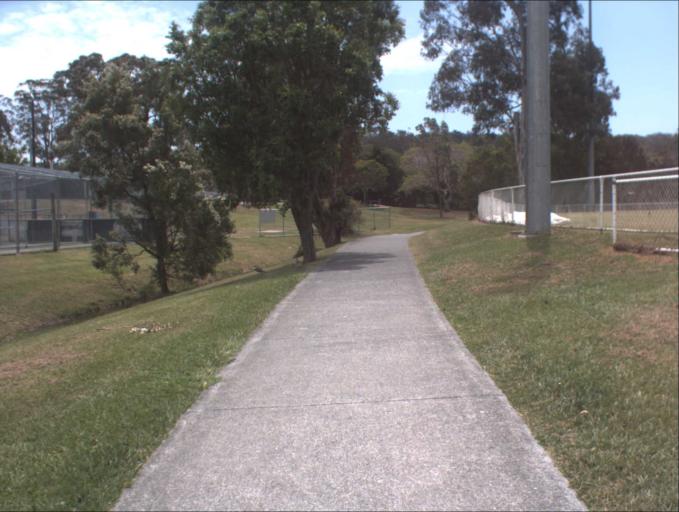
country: AU
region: Queensland
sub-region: Logan
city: Slacks Creek
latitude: -27.6446
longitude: 153.1668
